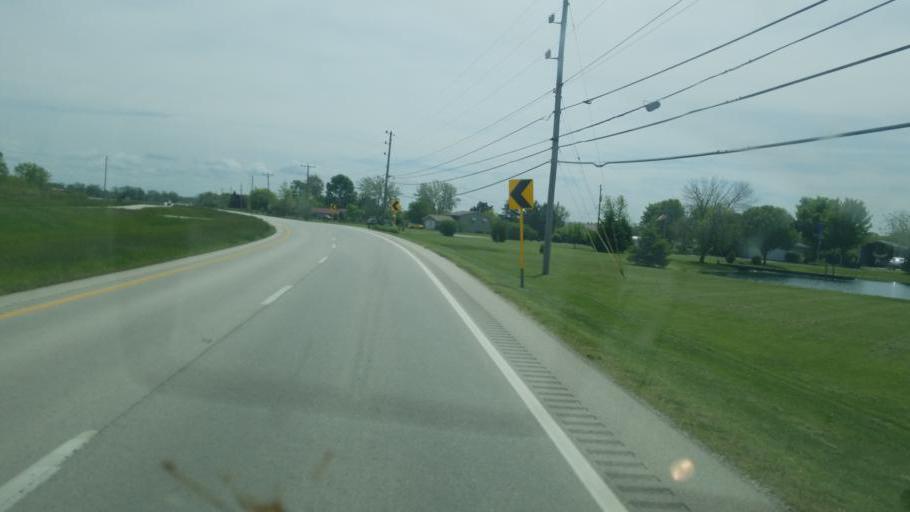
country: US
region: Ohio
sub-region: Ottawa County
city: Port Clinton
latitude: 41.5355
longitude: -83.0320
